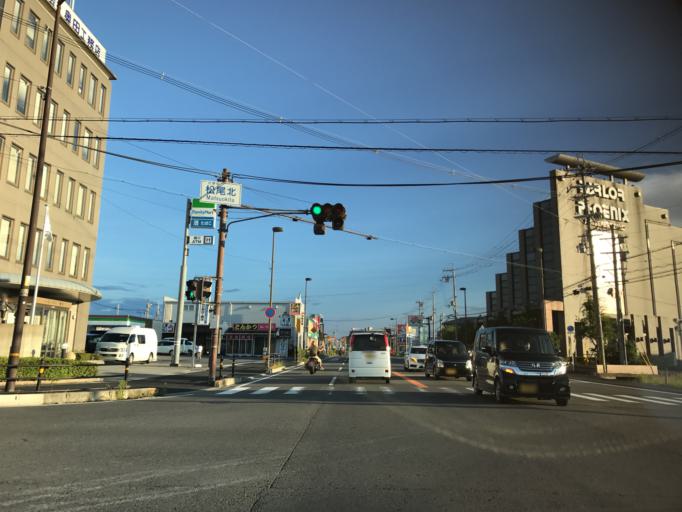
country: JP
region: Shiga Prefecture
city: Hino
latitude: 35.0206
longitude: 136.2390
